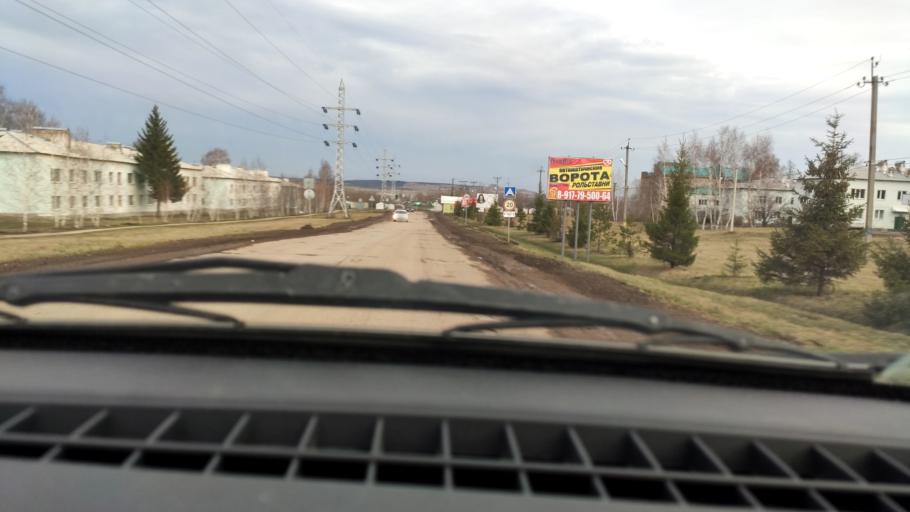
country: RU
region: Bashkortostan
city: Davlekanovo
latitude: 54.2247
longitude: 55.0386
